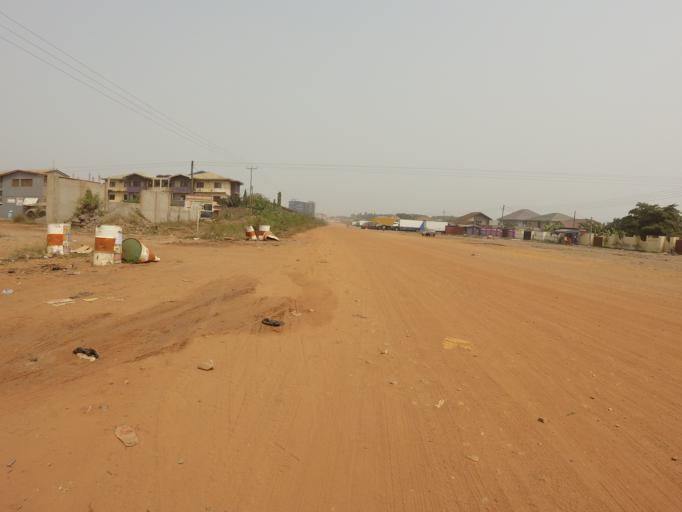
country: GH
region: Greater Accra
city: Nungua
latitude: 5.6453
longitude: -0.1039
